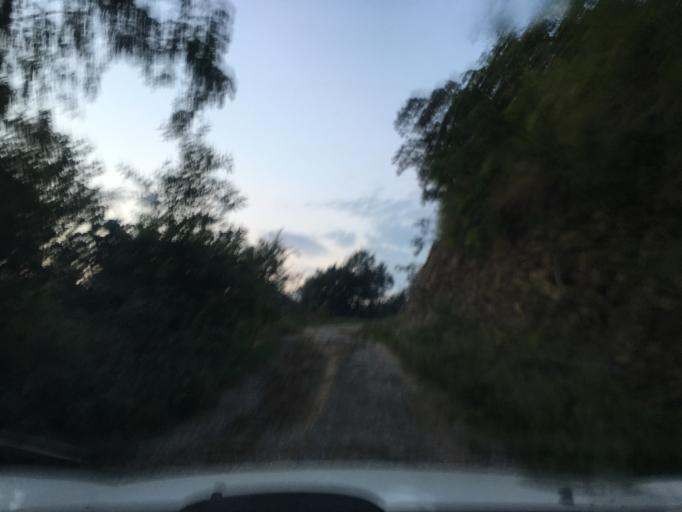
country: CN
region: Guangxi Zhuangzu Zizhiqu
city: Xinzhou
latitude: 25.3530
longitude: 105.7409
